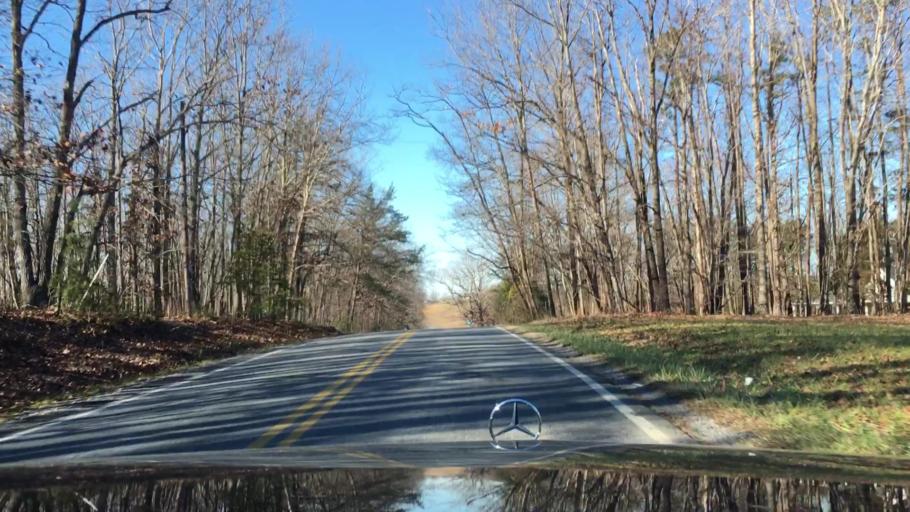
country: US
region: Virginia
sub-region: Pittsylvania County
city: Motley
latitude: 37.1847
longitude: -79.4173
